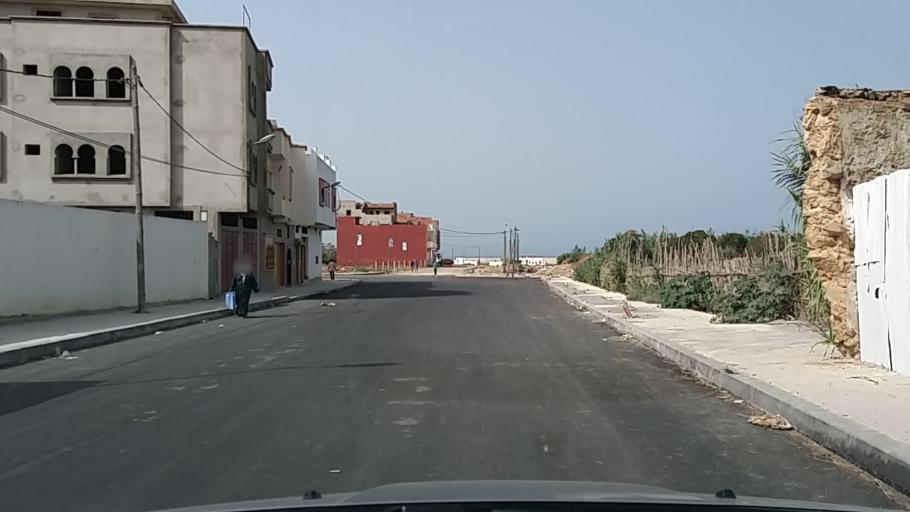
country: MA
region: Tanger-Tetouan
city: Asilah
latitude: 35.4623
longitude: -6.0414
